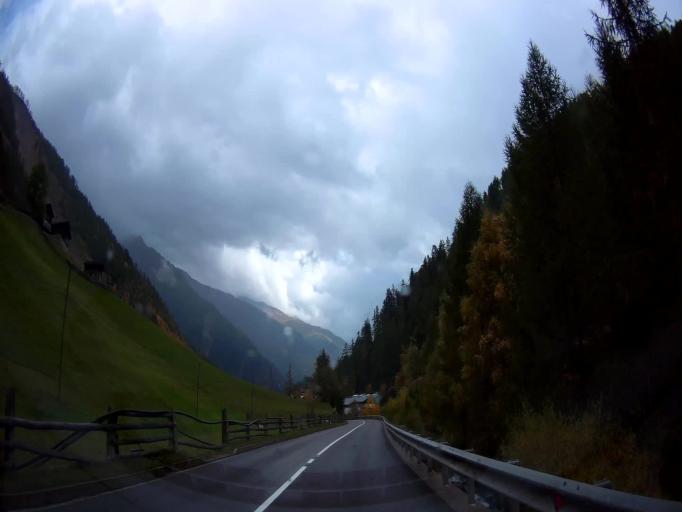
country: IT
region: Trentino-Alto Adige
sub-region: Bolzano
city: Senales
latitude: 46.7125
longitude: 10.8941
